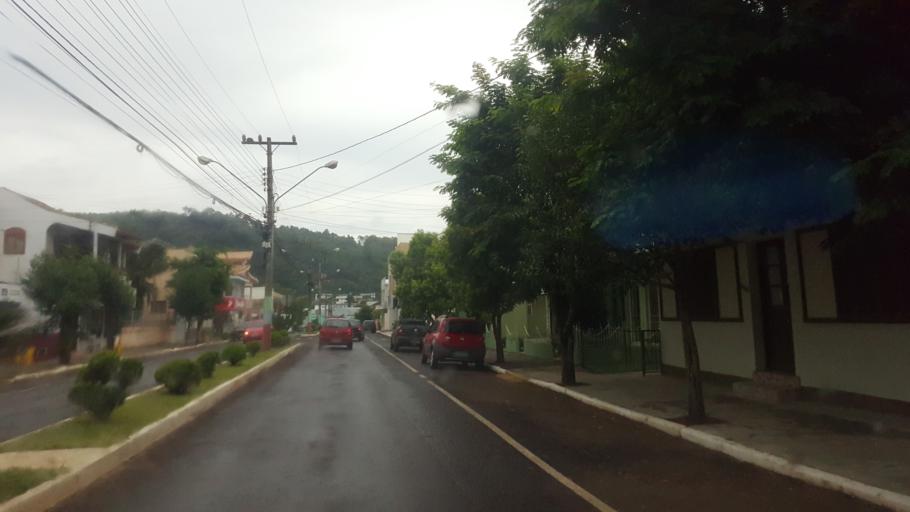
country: BR
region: Rio Grande do Sul
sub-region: Frederico Westphalen
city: Frederico Westphalen
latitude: -27.1043
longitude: -53.3991
